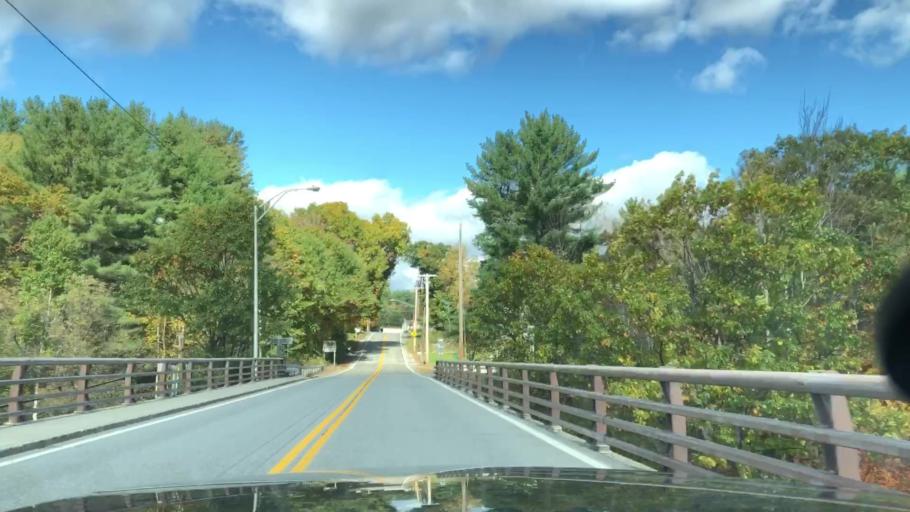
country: US
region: New York
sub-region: Warren County
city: Warrensburg
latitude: 43.7004
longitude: -73.9829
